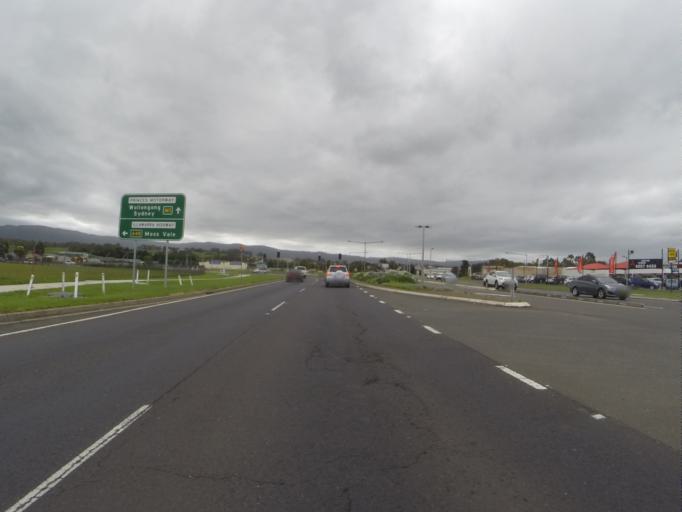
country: AU
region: New South Wales
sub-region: Shellharbour
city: Albion Park Rail
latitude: -34.5500
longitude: 150.7859
